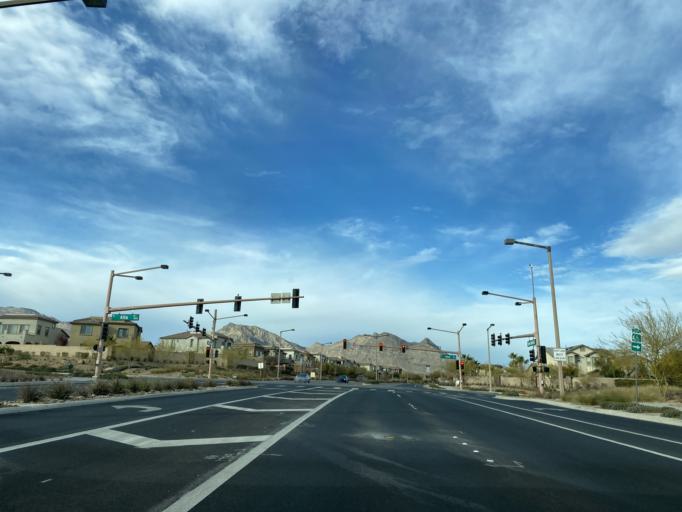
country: US
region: Nevada
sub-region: Clark County
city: Summerlin South
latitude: 36.1708
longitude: -115.3553
